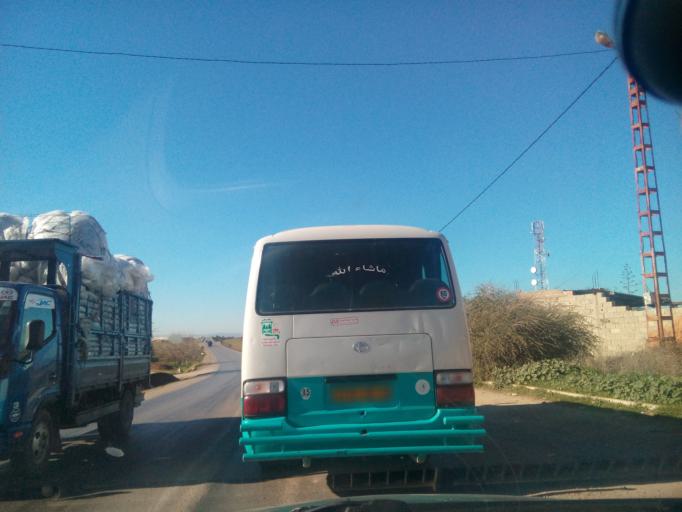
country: DZ
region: Relizane
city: Djidiouia
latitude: 35.8942
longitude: 0.7212
